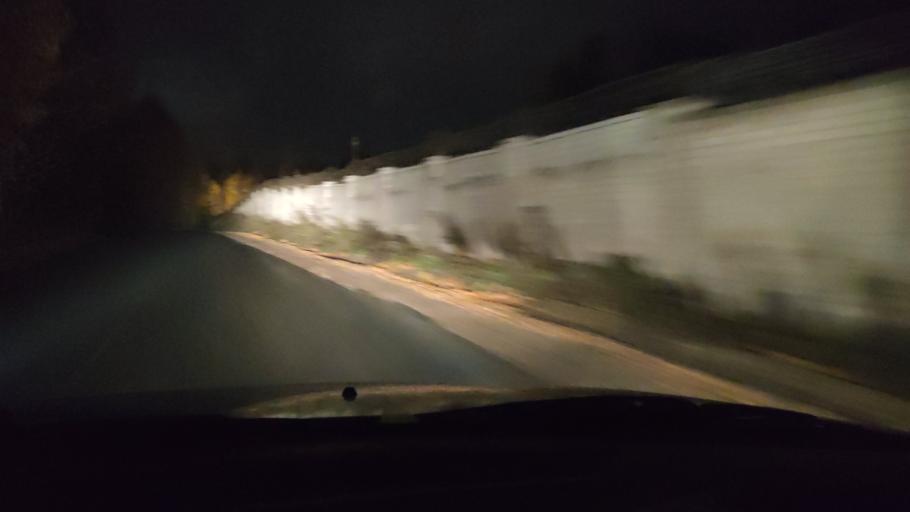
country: RU
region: Perm
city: Overyata
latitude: 58.0254
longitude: 55.9189
